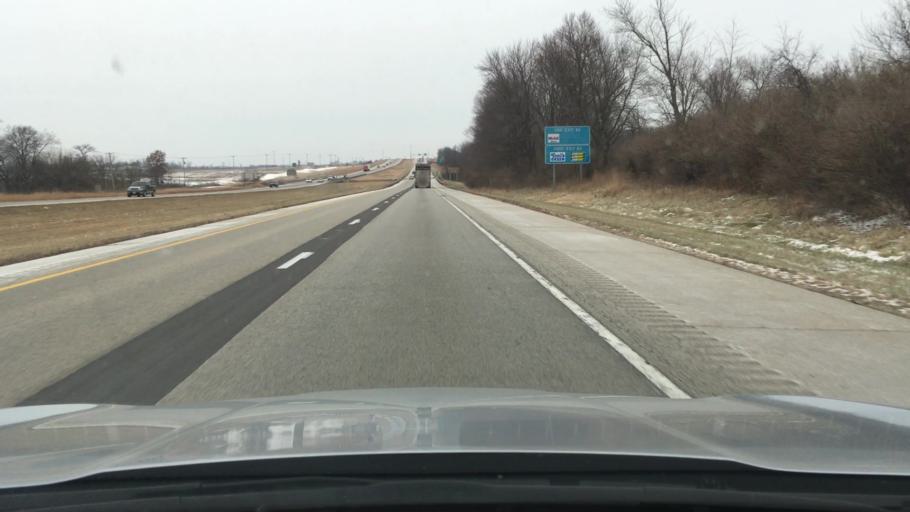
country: US
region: Illinois
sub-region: Sangamon County
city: Divernon
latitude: 39.5773
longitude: -89.6462
